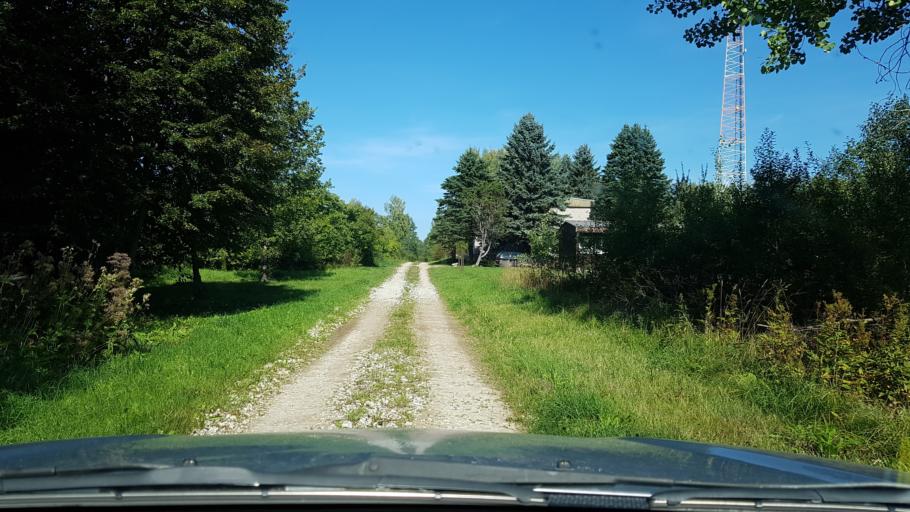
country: EE
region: Ida-Virumaa
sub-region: Sillamaee linn
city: Sillamae
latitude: 59.3272
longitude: 27.7754
